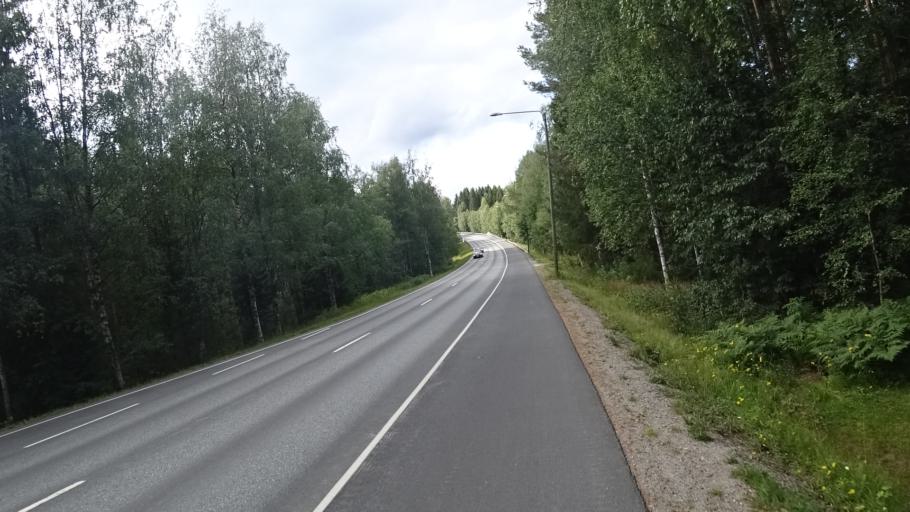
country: FI
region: North Karelia
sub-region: Joensuu
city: Ilomantsi
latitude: 62.6544
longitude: 30.9507
